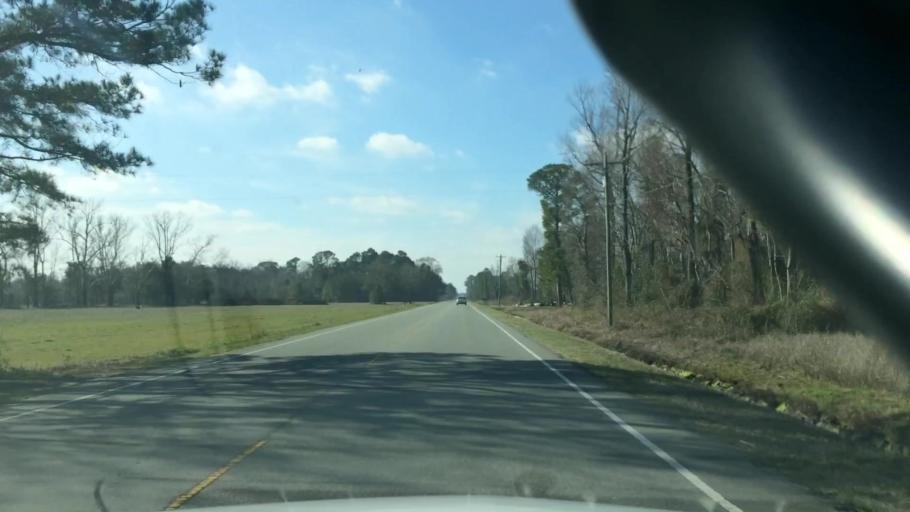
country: US
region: North Carolina
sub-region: Duplin County
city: Wallace
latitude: 34.7914
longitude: -77.8734
